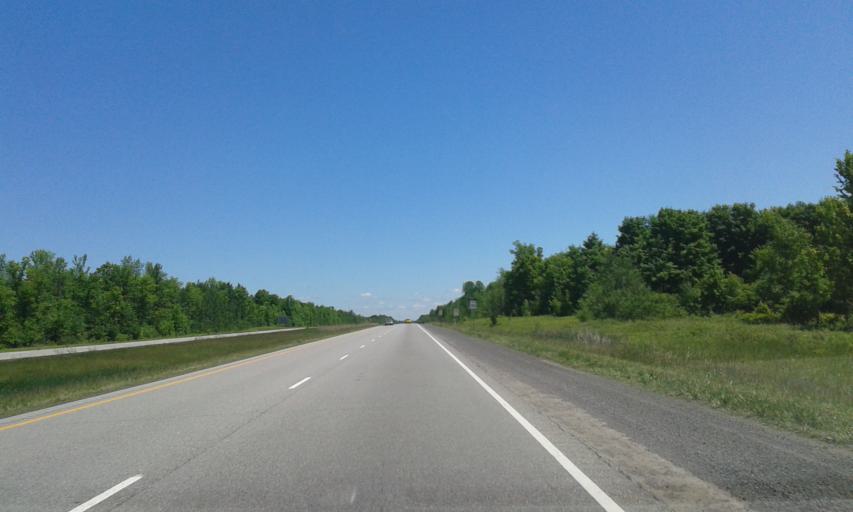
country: US
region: New York
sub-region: St. Lawrence County
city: Ogdensburg
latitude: 44.8353
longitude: -75.3655
